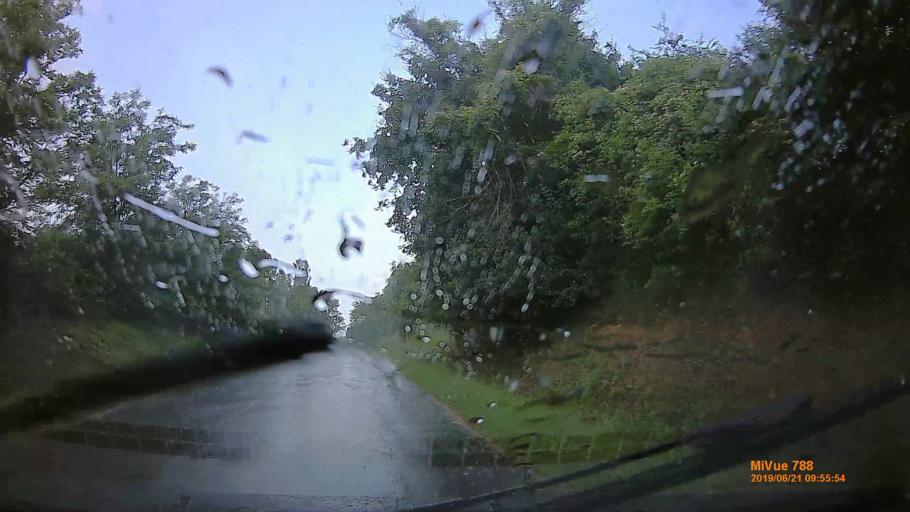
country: HU
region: Baranya
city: Buekkoesd
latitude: 46.2277
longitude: 17.9853
